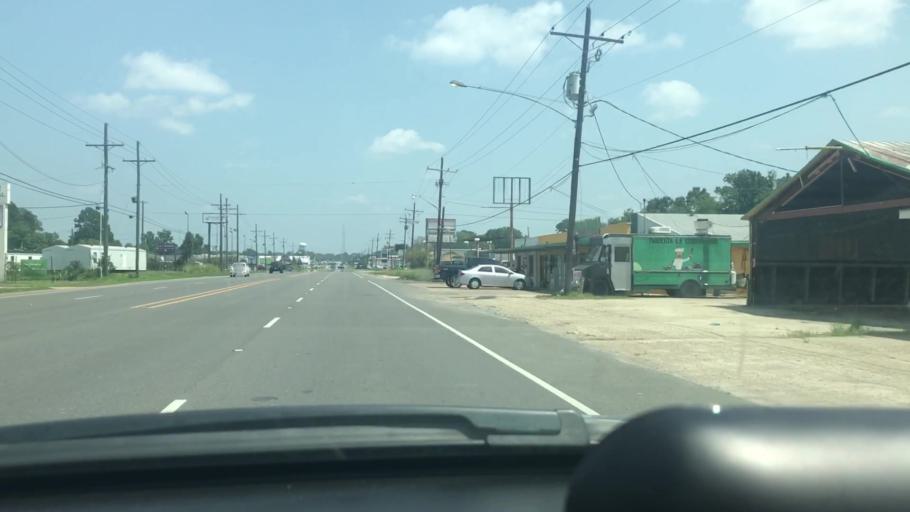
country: US
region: Louisiana
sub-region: Livingston Parish
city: Denham Springs
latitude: 30.4722
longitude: -90.9639
